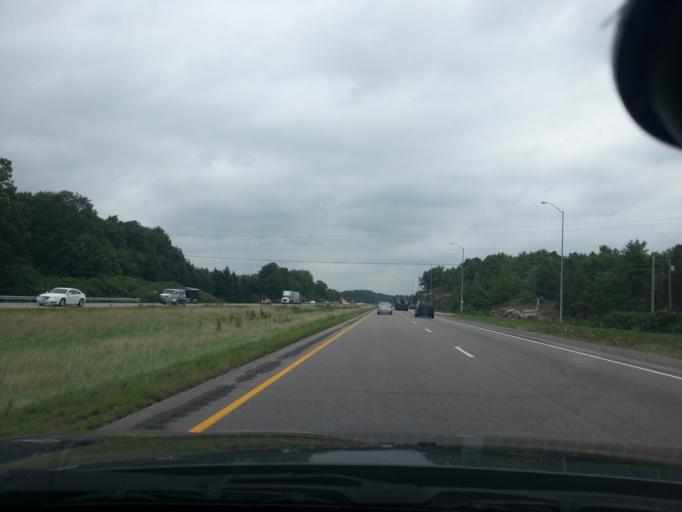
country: CA
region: Ontario
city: Brockville
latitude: 44.5072
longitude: -75.8357
